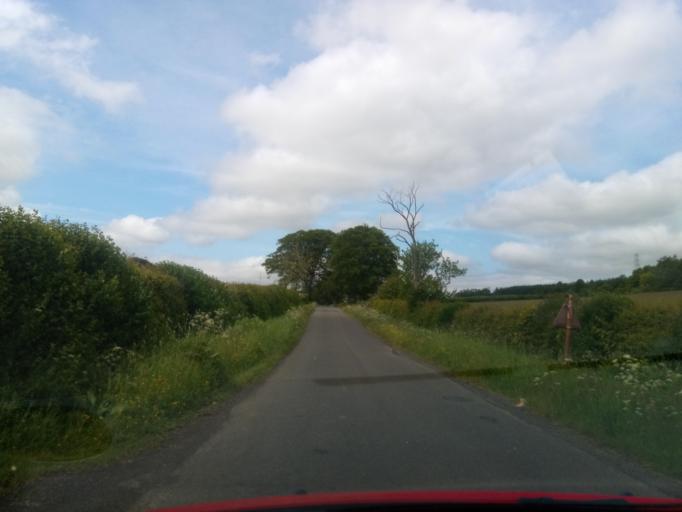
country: GB
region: Scotland
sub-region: The Scottish Borders
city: Selkirk
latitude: 55.5142
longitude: -2.7915
